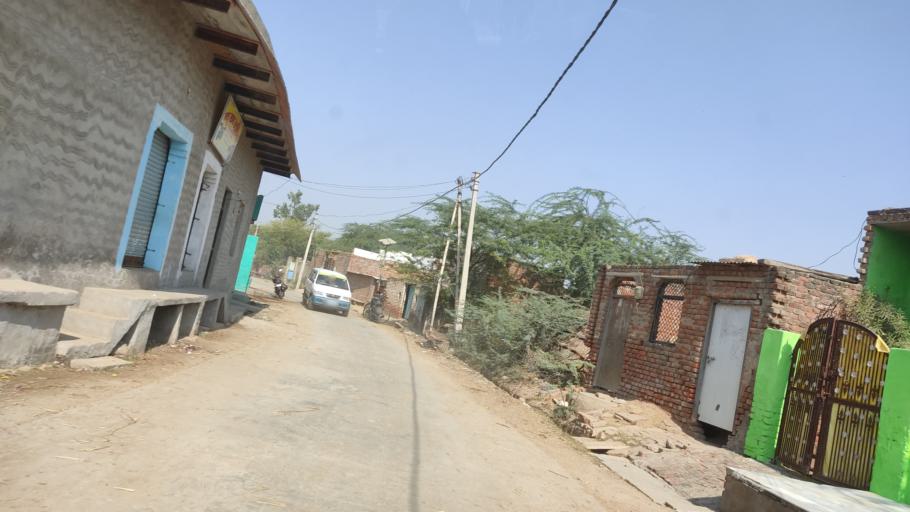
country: IN
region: Uttar Pradesh
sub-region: Mathura
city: Radha Kund
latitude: 27.5110
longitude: 77.4980
